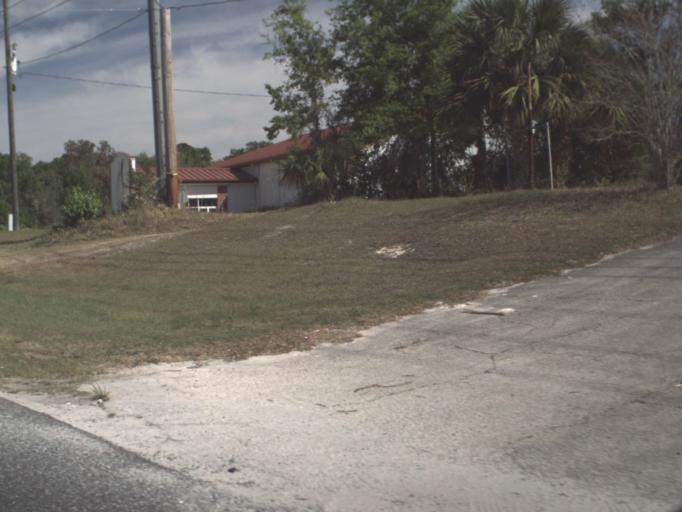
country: US
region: Florida
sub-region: Lake County
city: Lady Lake
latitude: 28.9050
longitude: -81.9154
